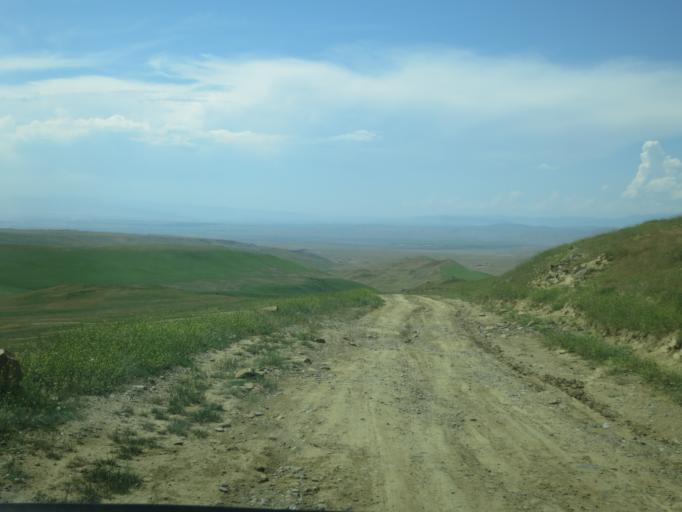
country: AZ
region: Agstafa
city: Saloglu
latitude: 41.4745
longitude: 45.3038
